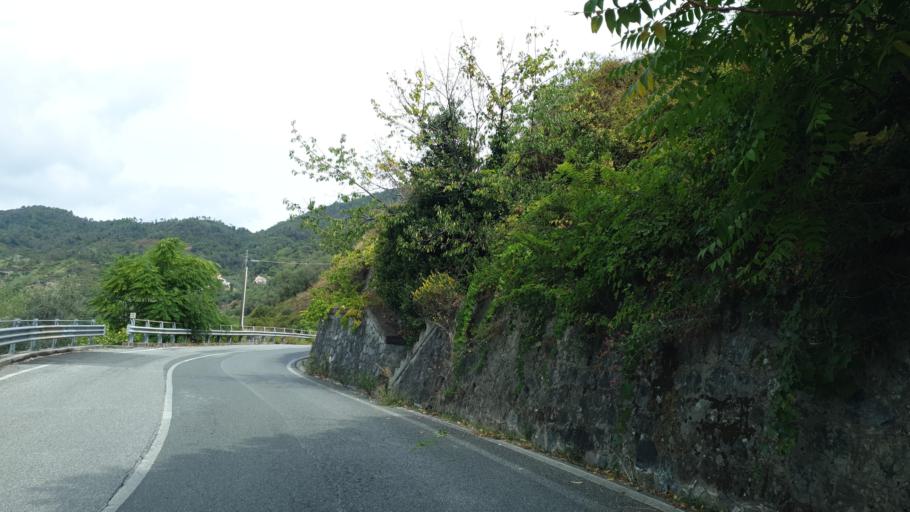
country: IT
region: Liguria
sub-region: Provincia di La Spezia
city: Levanto
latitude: 44.1894
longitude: 9.6276
